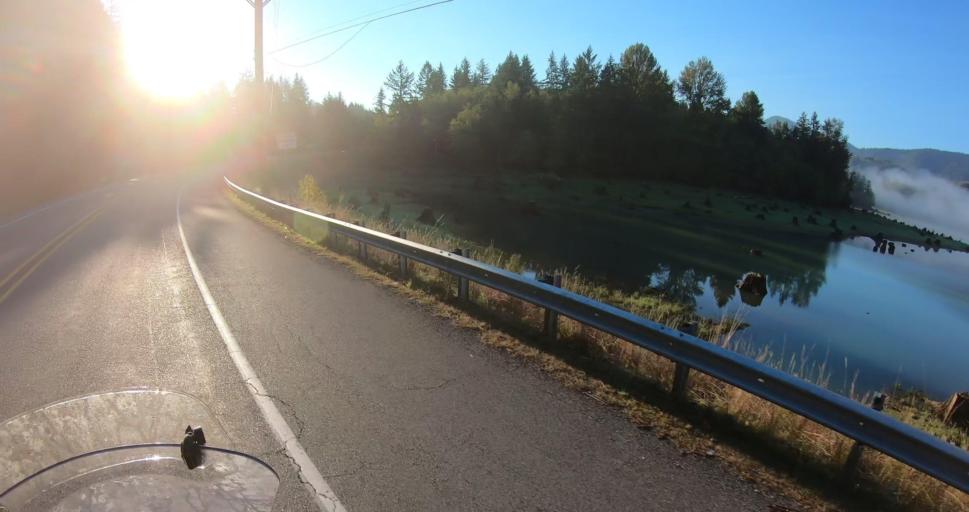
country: US
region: Washington
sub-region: Pierce County
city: Eatonville
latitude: 46.7953
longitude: -122.2755
